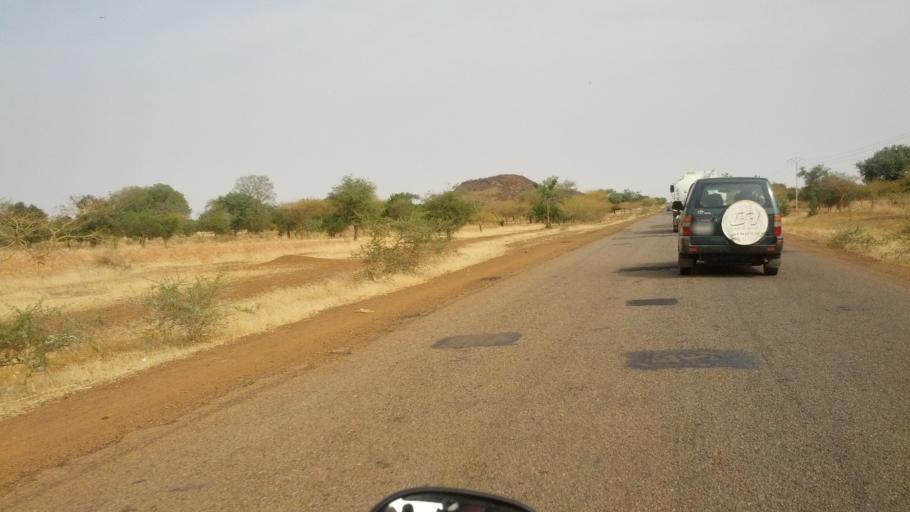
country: BF
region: Centre-Nord
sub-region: Province du Sanmatenga
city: Kaya
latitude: 12.9197
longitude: -1.0778
